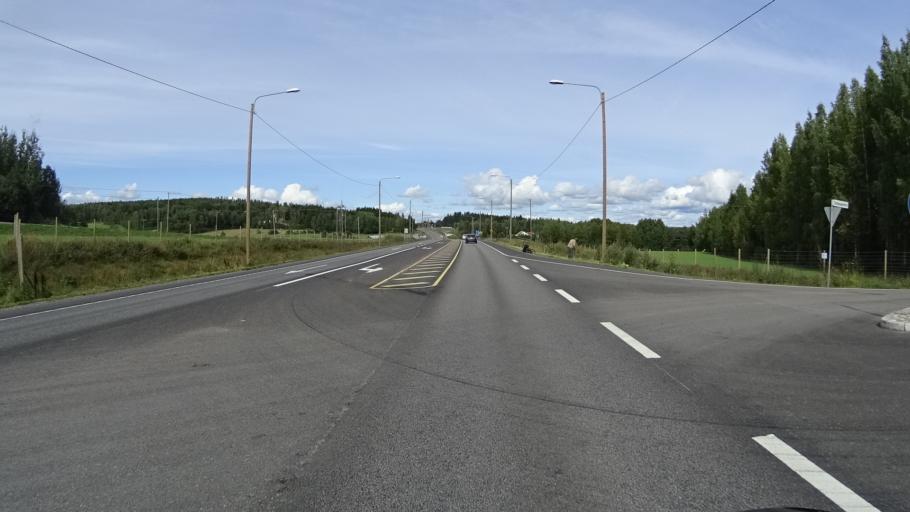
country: FI
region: Pirkanmaa
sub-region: Tampere
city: Haemeenkyroe
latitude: 61.6823
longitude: 23.1617
